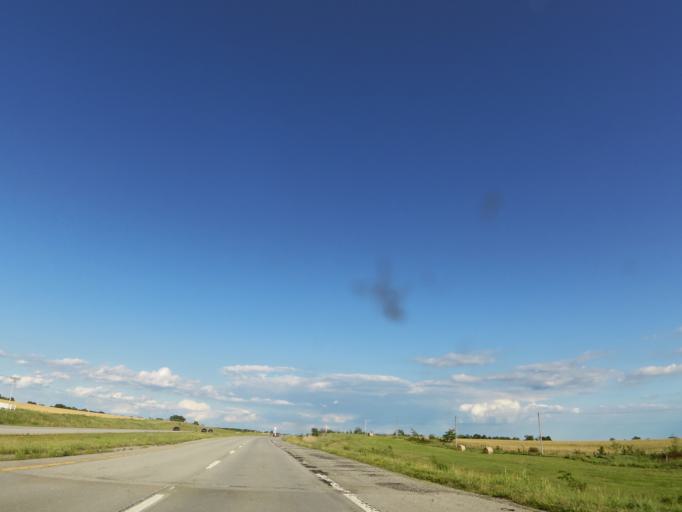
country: US
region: Missouri
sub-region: Pike County
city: Bowling Green
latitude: 39.2540
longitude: -91.0464
